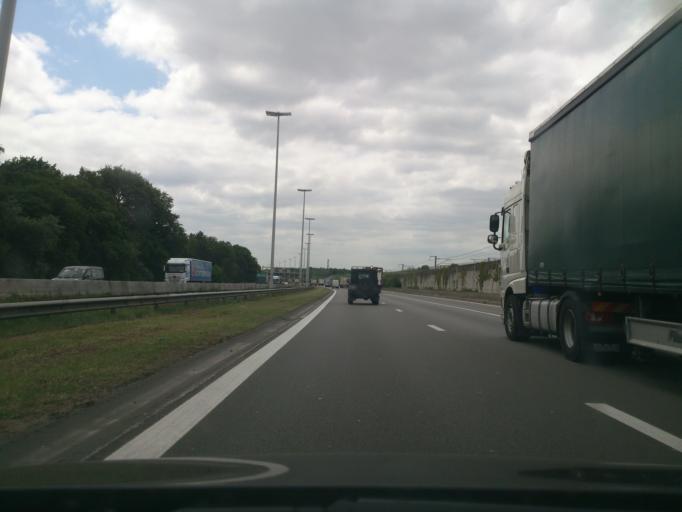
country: BE
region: Flanders
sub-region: Provincie Antwerpen
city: Brasschaat
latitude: 51.2908
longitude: 4.5203
